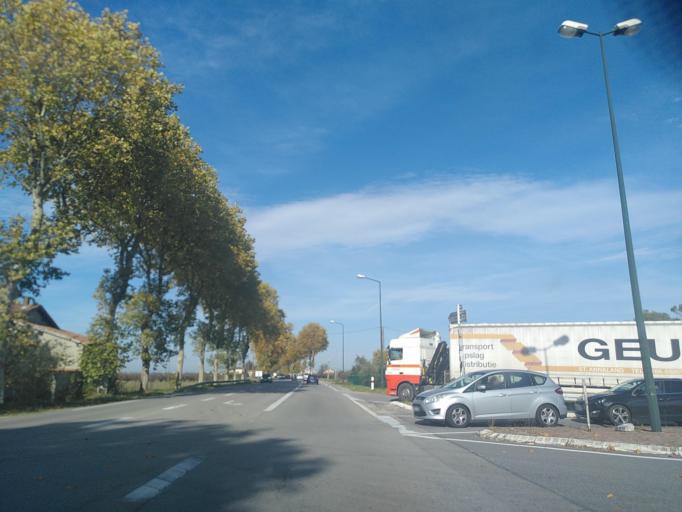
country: FR
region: Rhone-Alpes
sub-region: Departement de la Drome
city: Andancette
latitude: 45.2630
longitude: 4.8238
